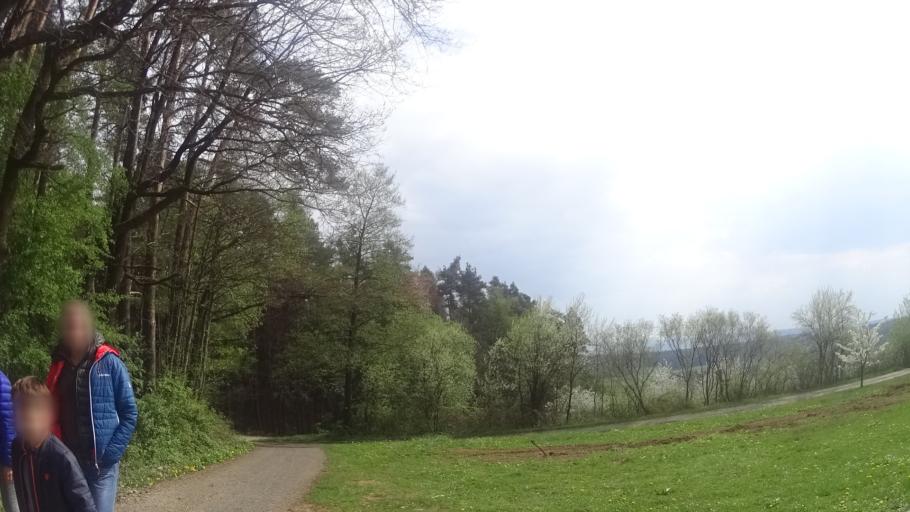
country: DE
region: Bavaria
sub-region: Upper Franconia
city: Igensdorf
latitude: 49.6241
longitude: 11.2116
